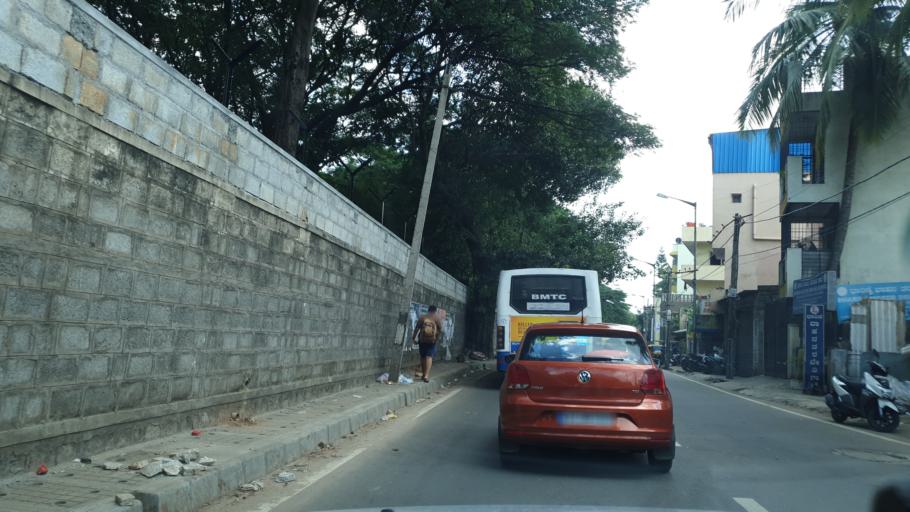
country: IN
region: Karnataka
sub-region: Bangalore Urban
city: Bangalore
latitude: 13.0258
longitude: 77.5621
